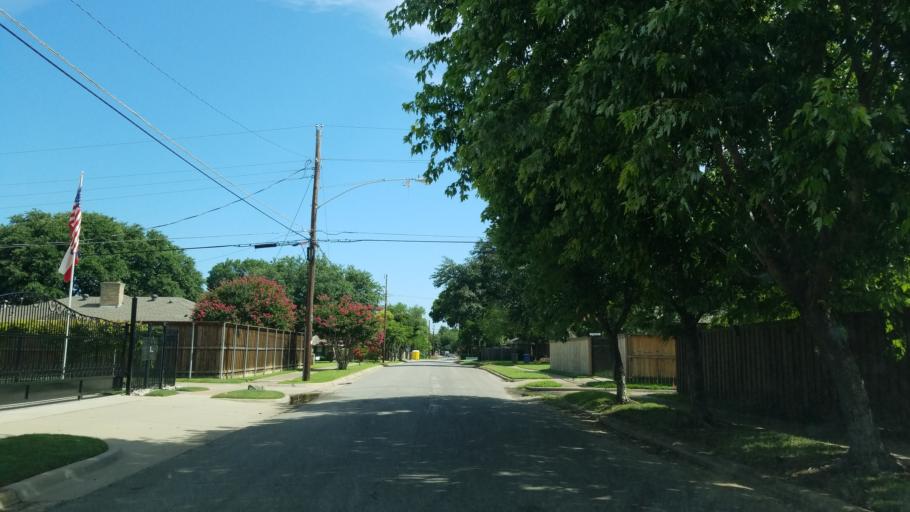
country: US
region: Texas
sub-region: Dallas County
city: Addison
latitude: 32.9082
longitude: -96.8434
